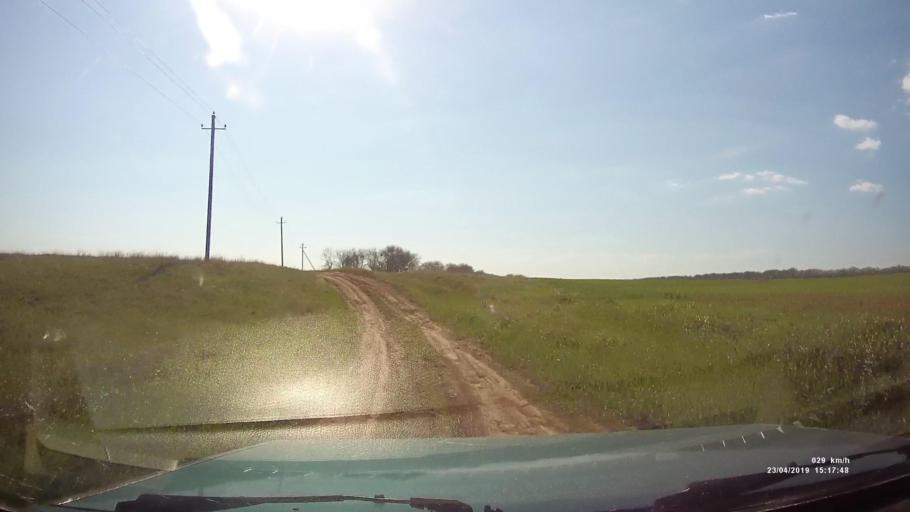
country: RU
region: Rostov
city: Remontnoye
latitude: 46.5282
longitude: 42.9673
